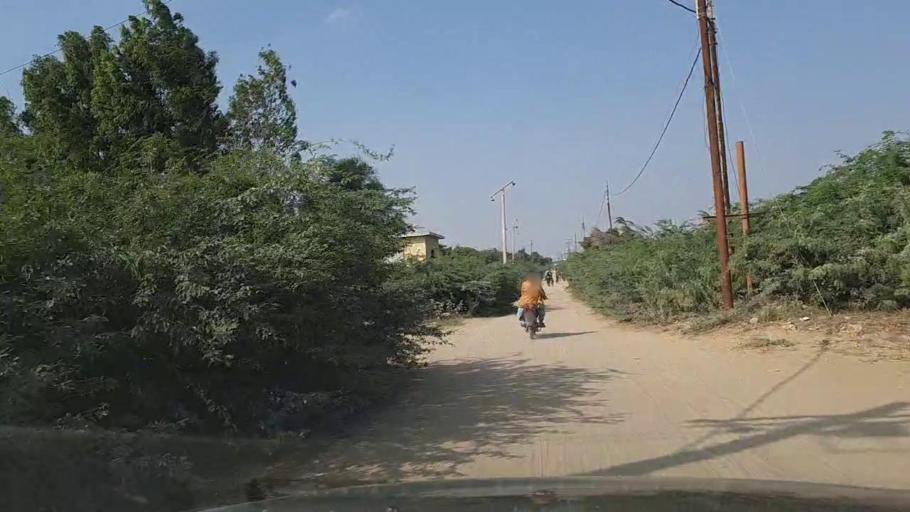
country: PK
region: Sindh
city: Gharo
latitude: 24.7483
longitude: 67.5822
